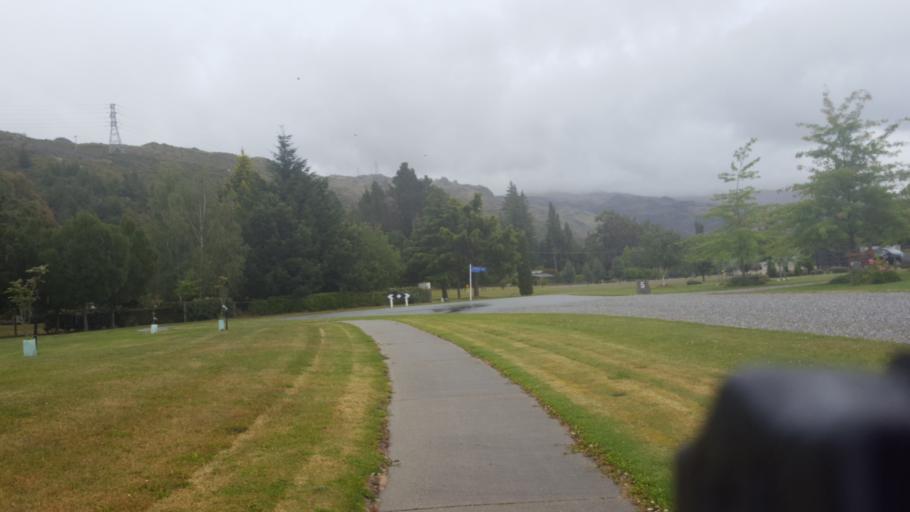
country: NZ
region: Otago
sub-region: Queenstown-Lakes District
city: Wanaka
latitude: -45.1953
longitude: 169.3161
